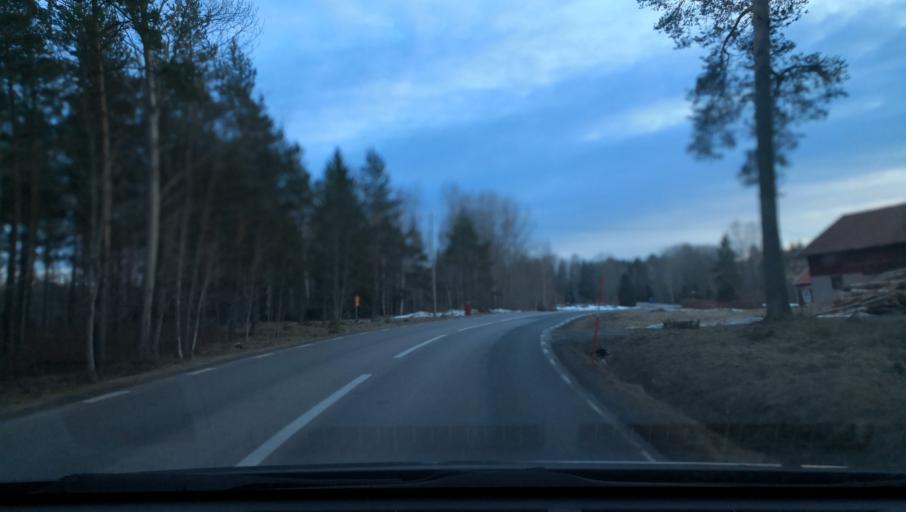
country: SE
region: Uppsala
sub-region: Osthammars Kommun
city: Osterbybruk
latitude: 60.2648
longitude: 17.9549
